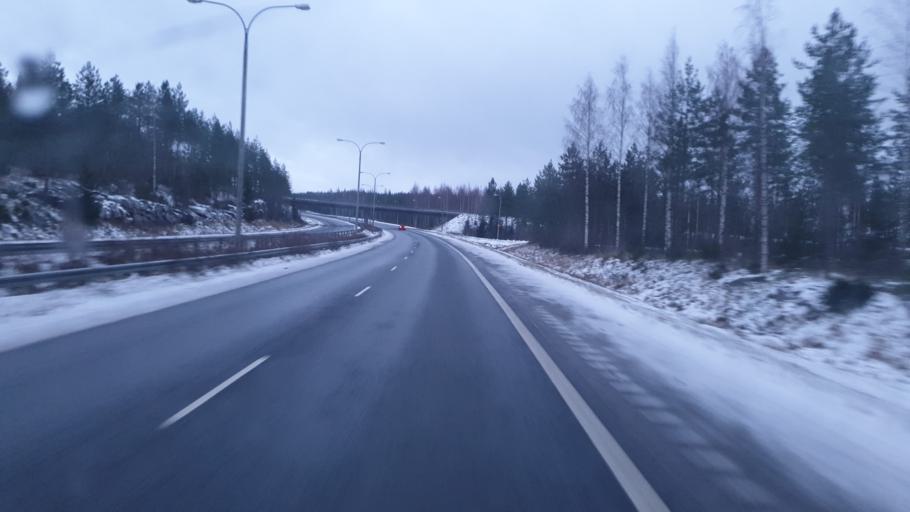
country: FI
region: Northern Savo
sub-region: Kuopio
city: Siilinjaervi
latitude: 63.0197
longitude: 27.6615
